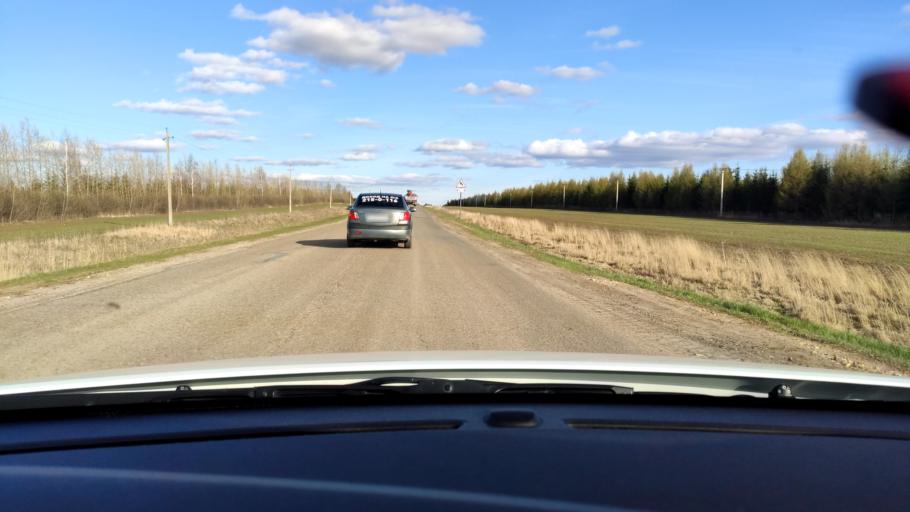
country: RU
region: Tatarstan
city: Vysokaya Gora
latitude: 55.8934
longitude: 49.3379
